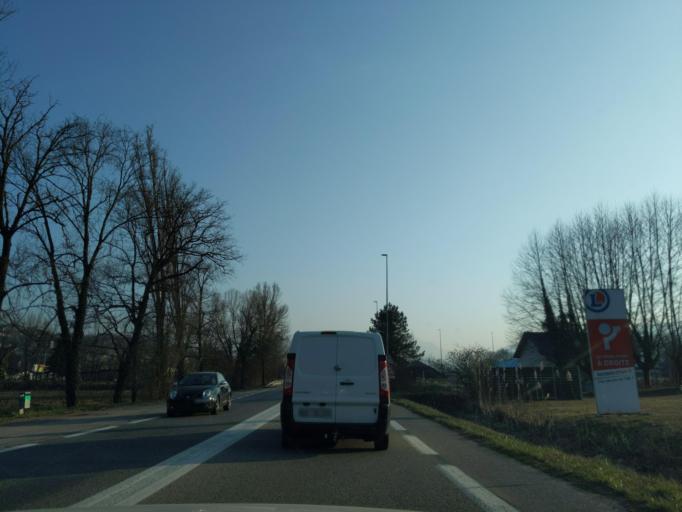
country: FR
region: Rhone-Alpes
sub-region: Departement de la Savoie
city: Voglans
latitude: 45.6390
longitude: 5.8923
